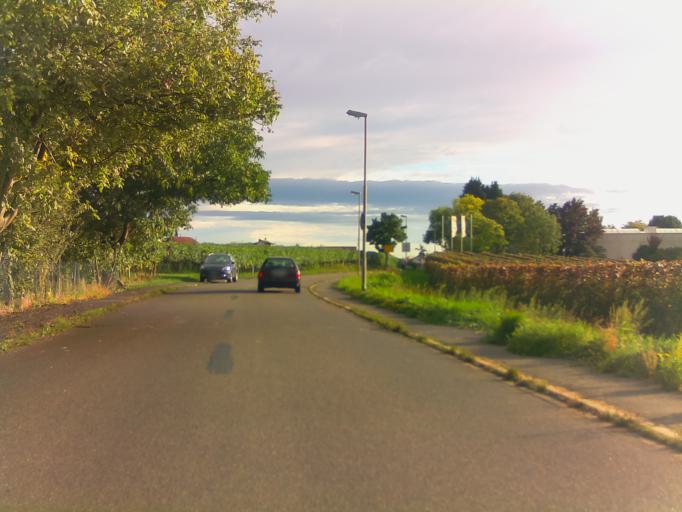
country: DE
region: Baden-Wuerttemberg
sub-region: Karlsruhe Region
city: Weinheim
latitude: 49.5165
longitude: 8.6660
